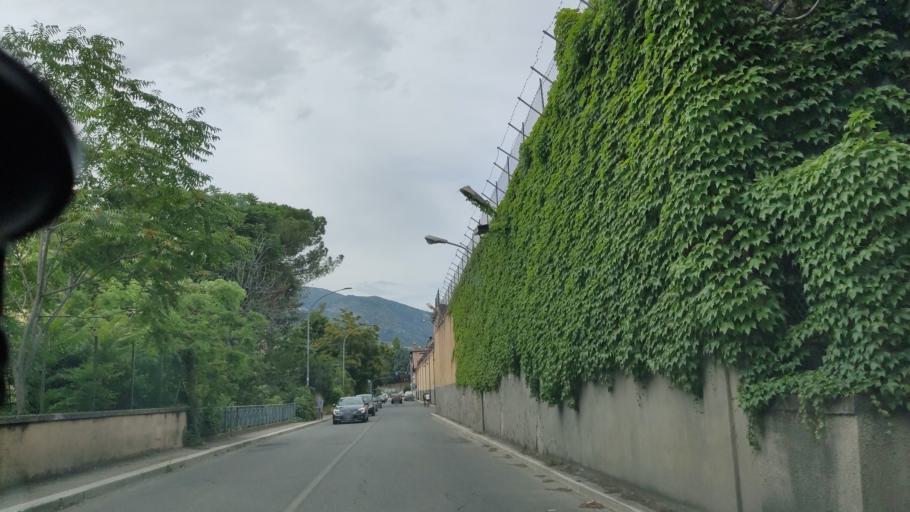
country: IT
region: Umbria
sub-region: Provincia di Terni
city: Terni
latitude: 42.5626
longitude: 12.6583
